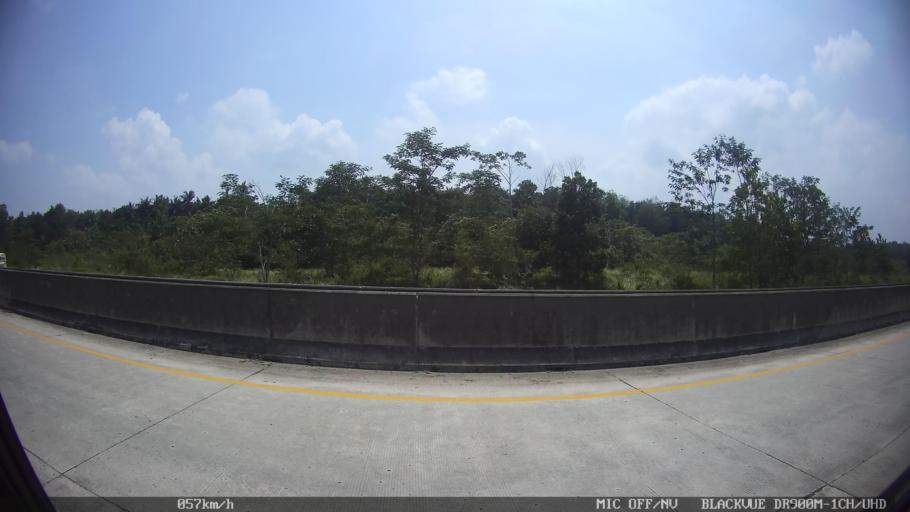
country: ID
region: Lampung
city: Kedaton
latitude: -5.3859
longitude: 105.3378
